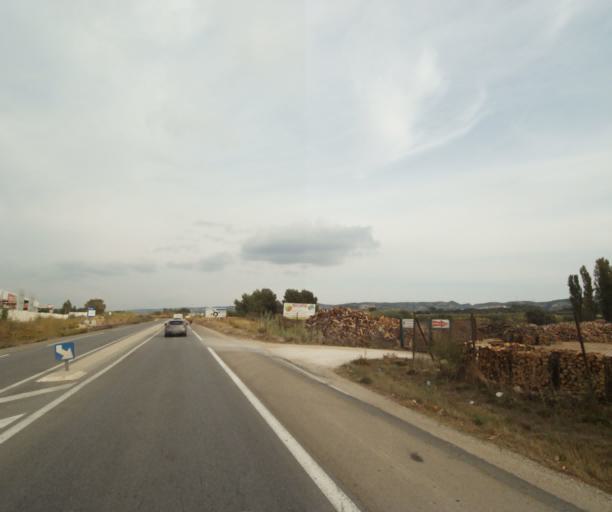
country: FR
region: Provence-Alpes-Cote d'Azur
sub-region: Departement des Bouches-du-Rhone
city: Marignane
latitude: 43.3937
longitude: 5.1997
